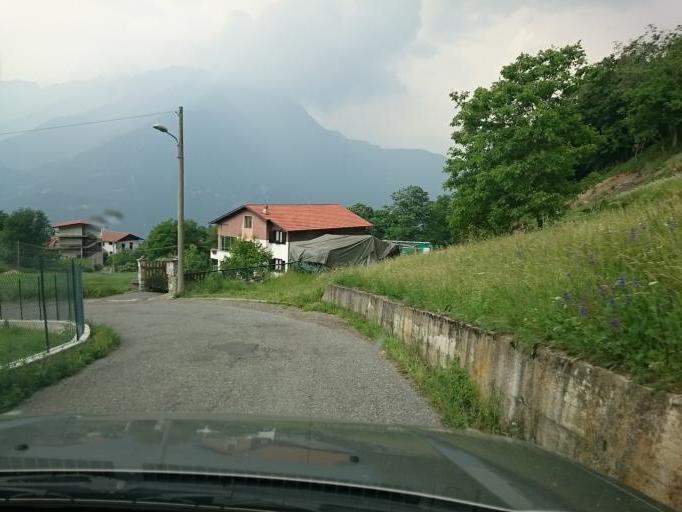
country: IT
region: Lombardy
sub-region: Provincia di Brescia
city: Paspardo
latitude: 46.0364
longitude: 10.3677
